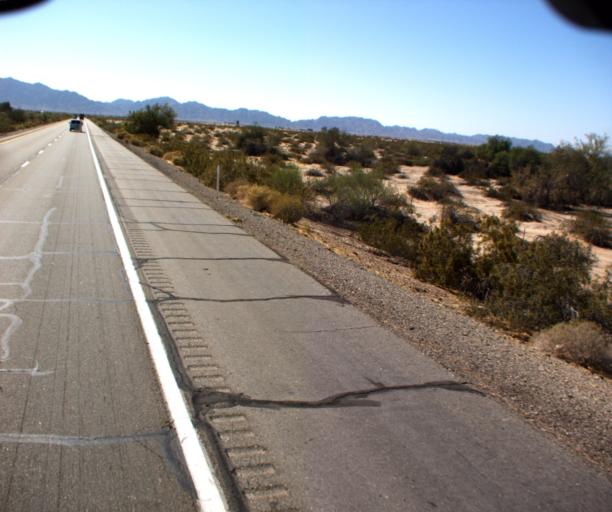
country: US
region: Arizona
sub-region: Yuma County
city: Wellton
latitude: 32.6538
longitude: -114.1771
